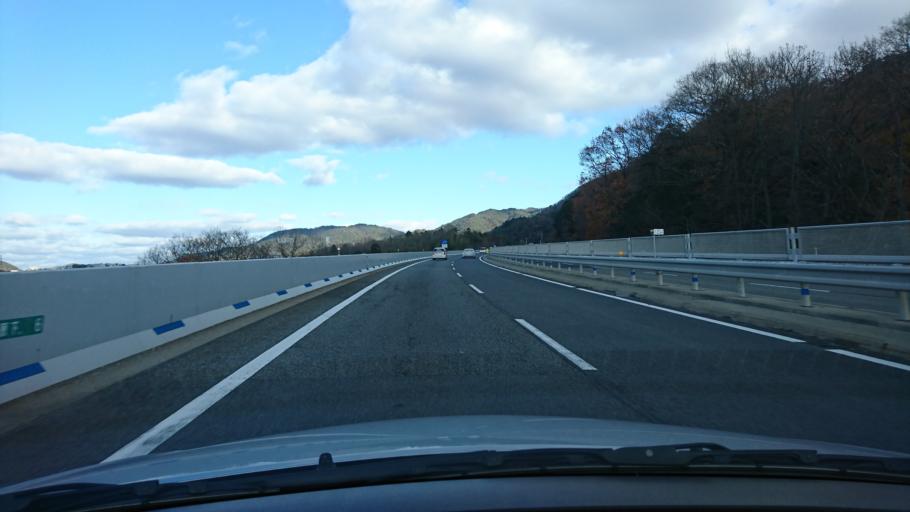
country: JP
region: Hyogo
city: Kobe
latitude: 34.7615
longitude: 135.1778
